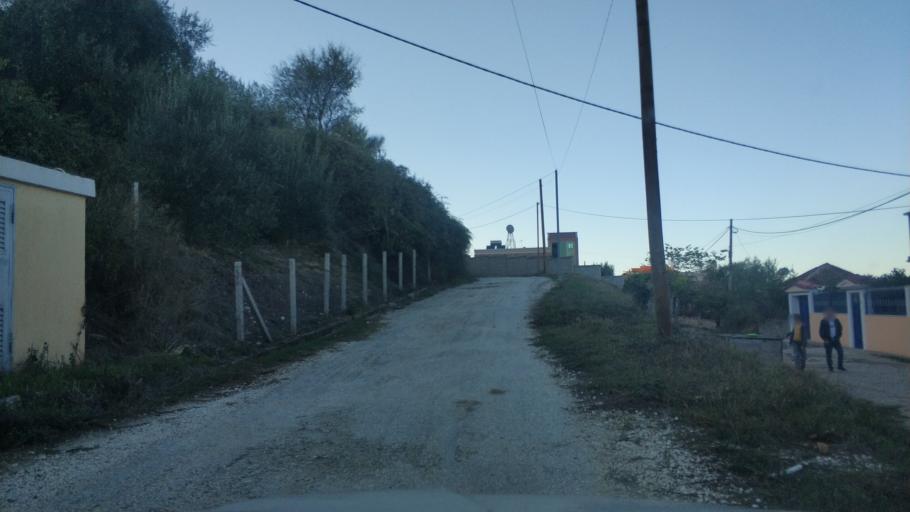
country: AL
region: Vlore
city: Vlore
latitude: 40.5134
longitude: 19.4195
